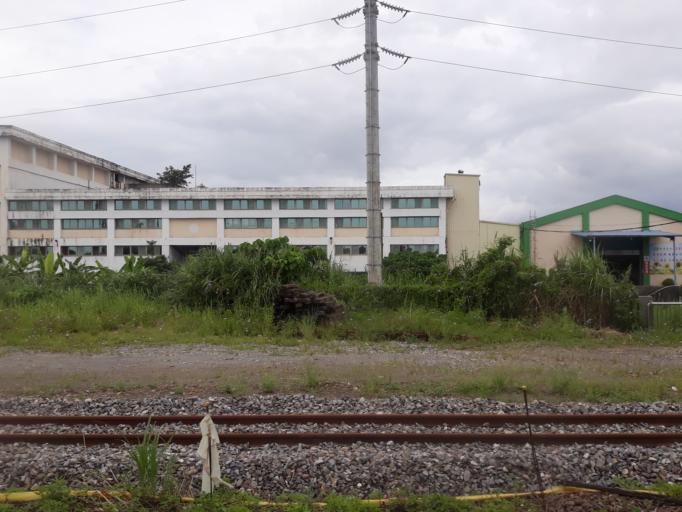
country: TW
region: Taiwan
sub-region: Yilan
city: Yilan
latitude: 24.6960
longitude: 121.7752
